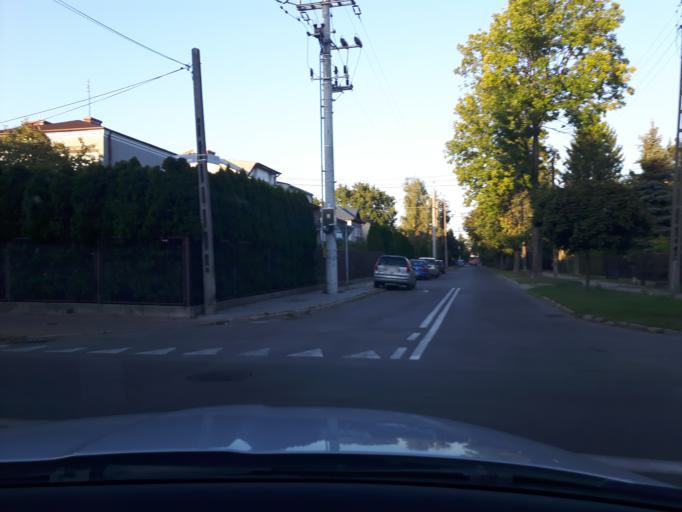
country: PL
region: Masovian Voivodeship
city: Zielonka
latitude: 52.3050
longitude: 21.1589
